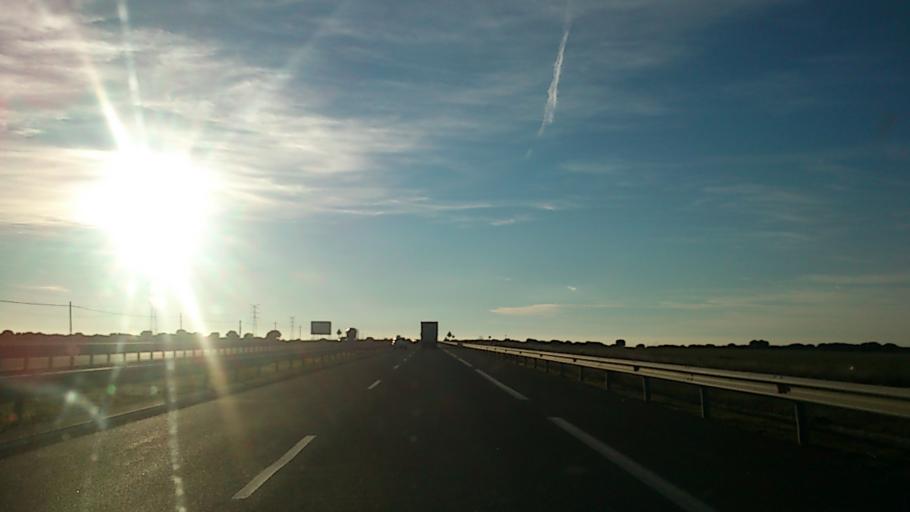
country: ES
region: Castille-La Mancha
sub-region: Provincia de Guadalajara
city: Ledanca
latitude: 40.8520
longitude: -2.8557
